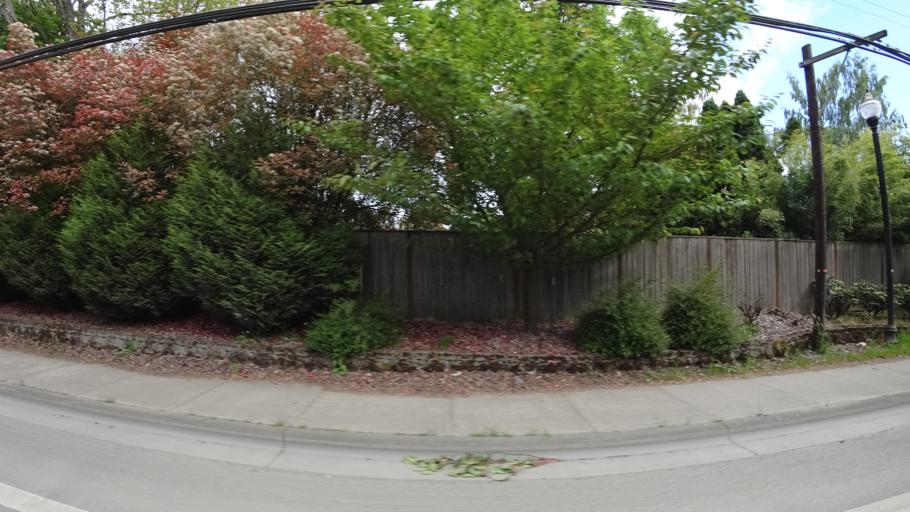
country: US
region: Oregon
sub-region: Washington County
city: Hillsboro
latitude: 45.5002
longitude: -122.9654
